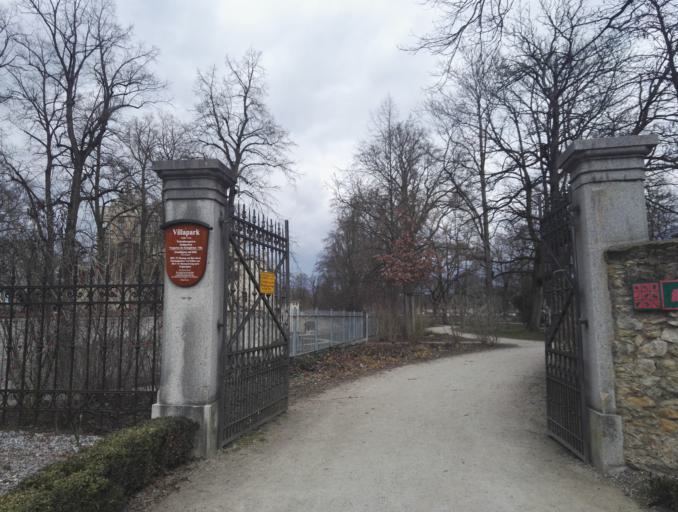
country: DE
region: Bavaria
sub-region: Upper Palatinate
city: Regensburg
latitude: 49.0181
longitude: 12.1085
